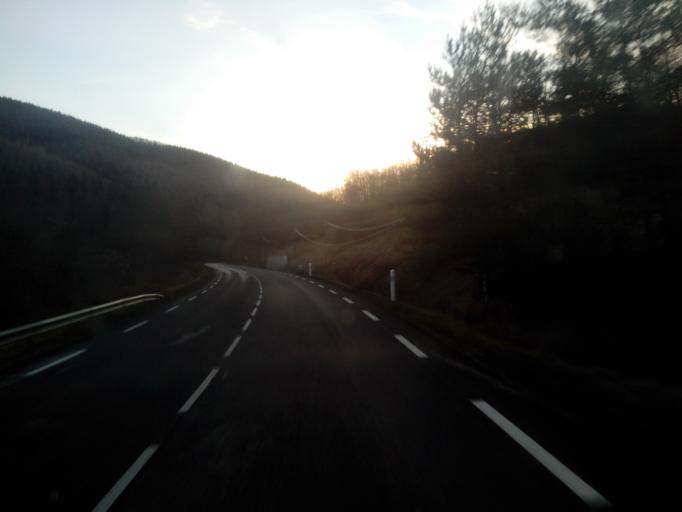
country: FR
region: Midi-Pyrenees
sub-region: Departement de l'Ariege
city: Saint-Paul-de-Jarrat
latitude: 42.9313
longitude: 1.7068
